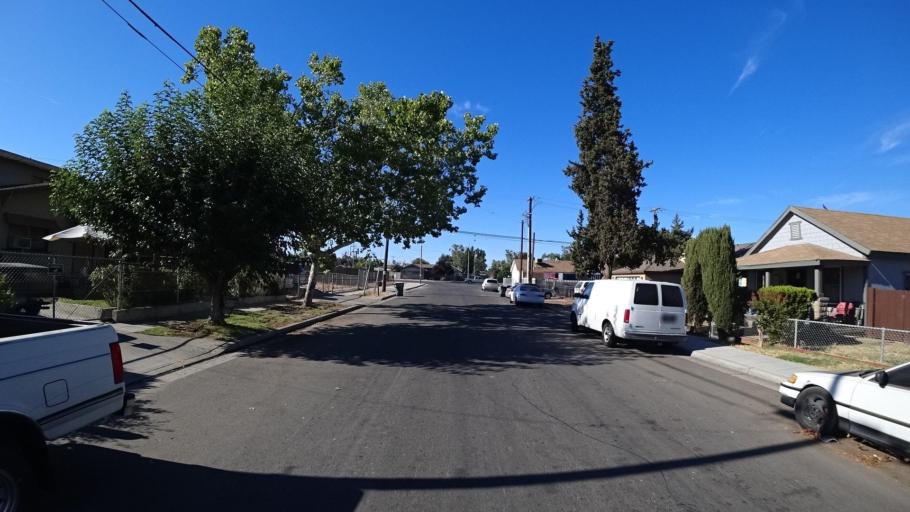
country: US
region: California
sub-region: Fresno County
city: Fresno
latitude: 36.7512
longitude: -119.7680
